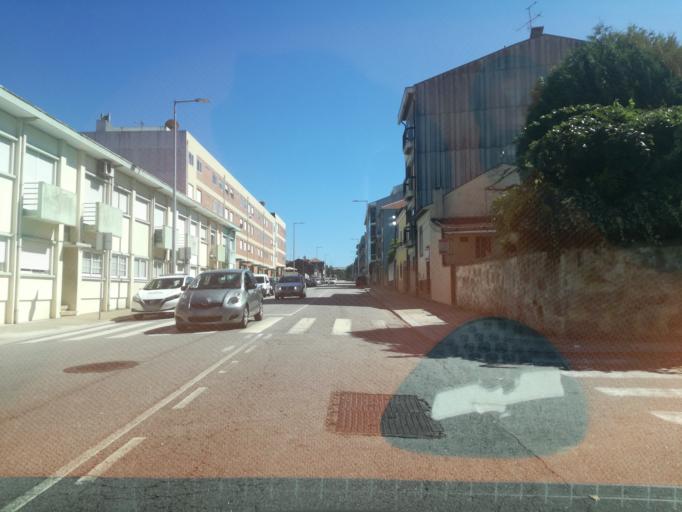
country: PT
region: Porto
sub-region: Matosinhos
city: Sao Mamede de Infesta
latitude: 41.1838
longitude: -8.6096
